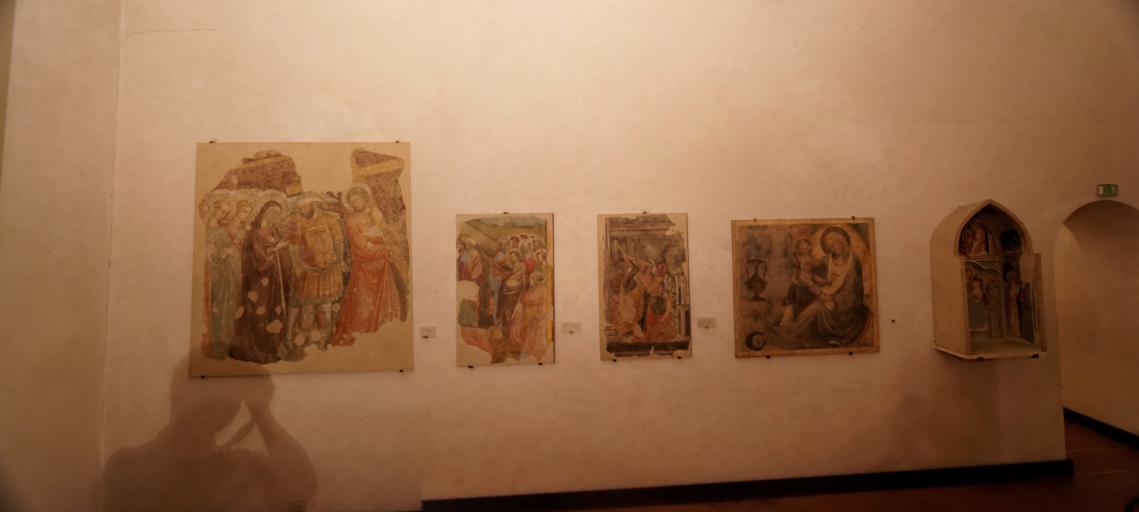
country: IT
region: Tuscany
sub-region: Province of Florence
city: Florence
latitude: 43.7677
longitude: 11.2624
